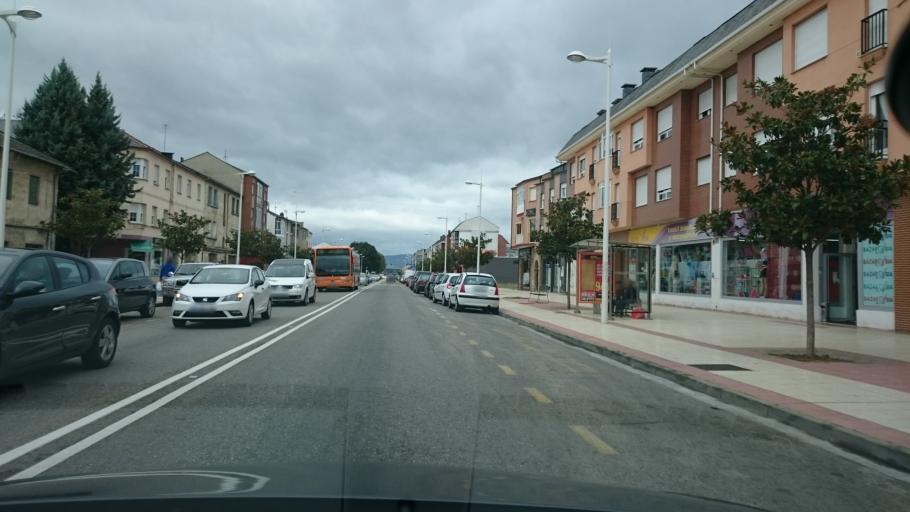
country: ES
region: Castille and Leon
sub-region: Provincia de Leon
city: Ponferrada
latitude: 42.5608
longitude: -6.6264
